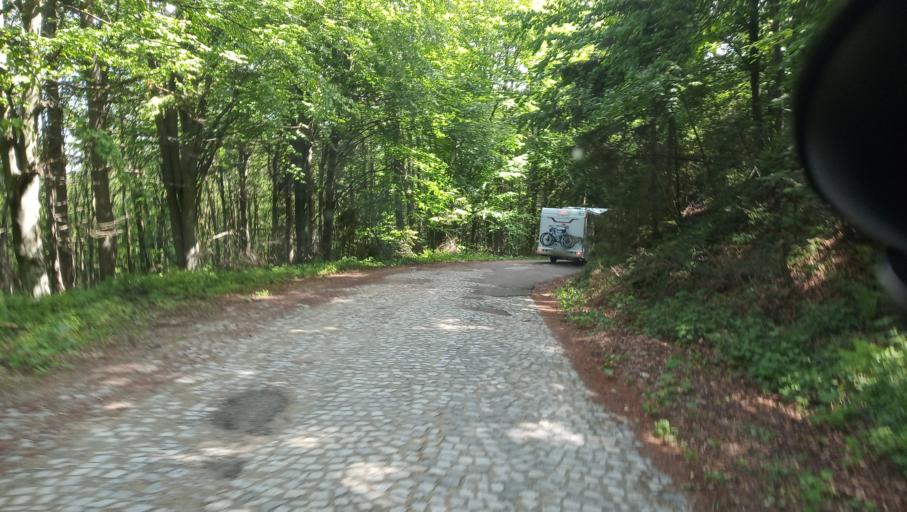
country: RO
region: Caras-Severin
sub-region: Comuna Valiug
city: Valiug
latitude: 45.2165
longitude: 22.0626
